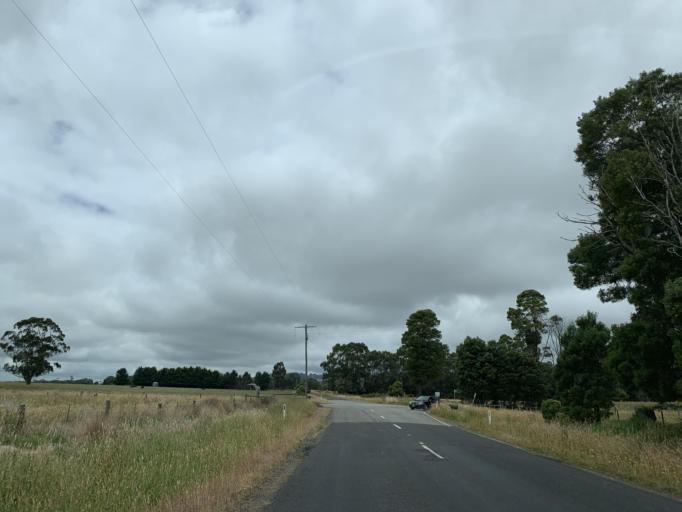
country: AU
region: Victoria
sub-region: Baw Baw
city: Warragul
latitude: -38.2445
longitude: 145.9737
